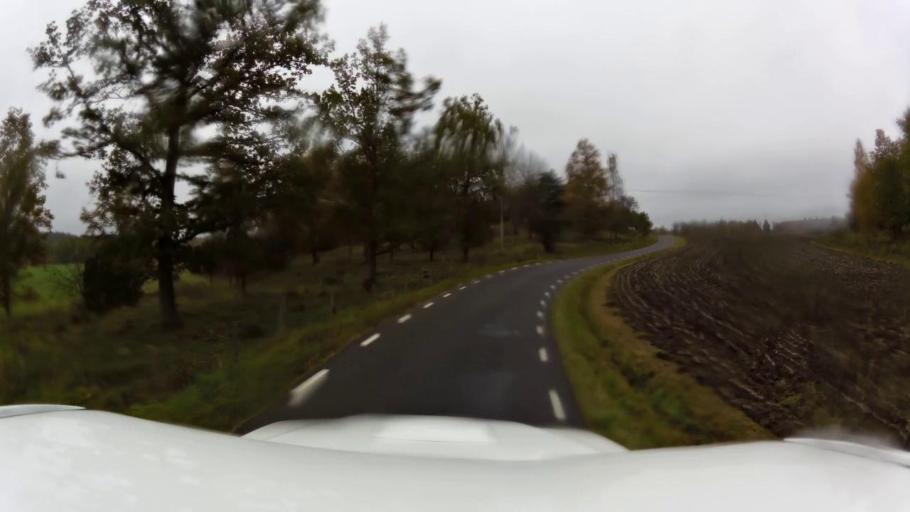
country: SE
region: OEstergoetland
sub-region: Linkopings Kommun
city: Linghem
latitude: 58.3507
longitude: 15.8804
